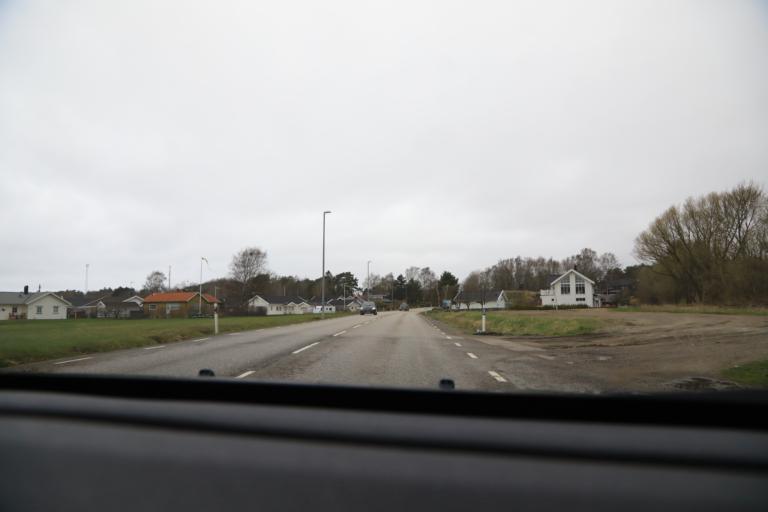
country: SE
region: Halland
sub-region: Kungsbacka Kommun
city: Frillesas
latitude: 57.3130
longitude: 12.1797
